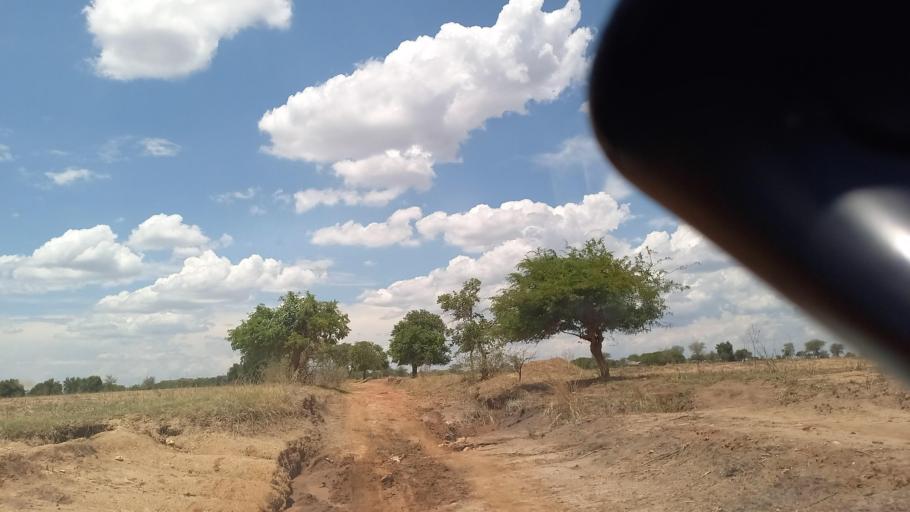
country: ZM
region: Southern
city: Mazabuka
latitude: -16.1135
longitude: 27.8145
